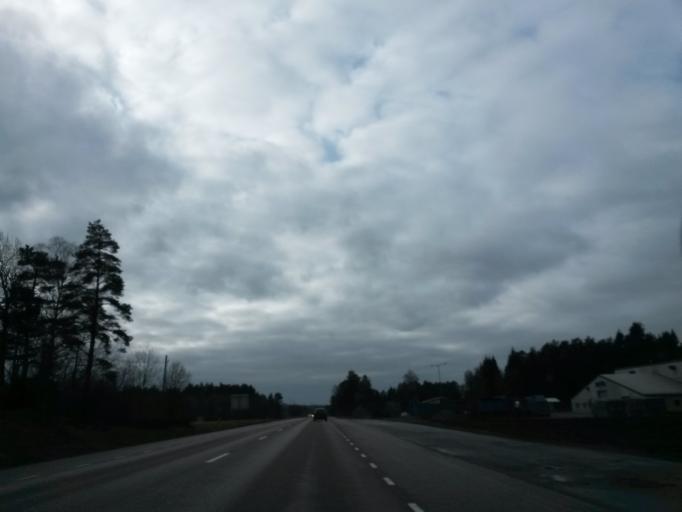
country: SE
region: Vaestra Goetaland
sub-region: Vargarda Kommun
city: Jonstorp
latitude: 57.9866
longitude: 12.6939
